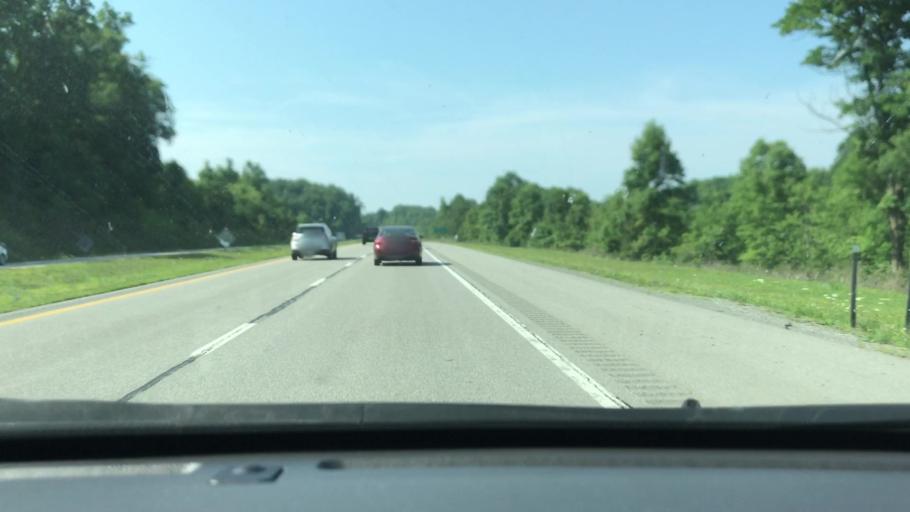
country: US
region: West Virginia
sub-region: Nicholas County
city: Summersville
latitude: 38.2573
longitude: -80.8567
